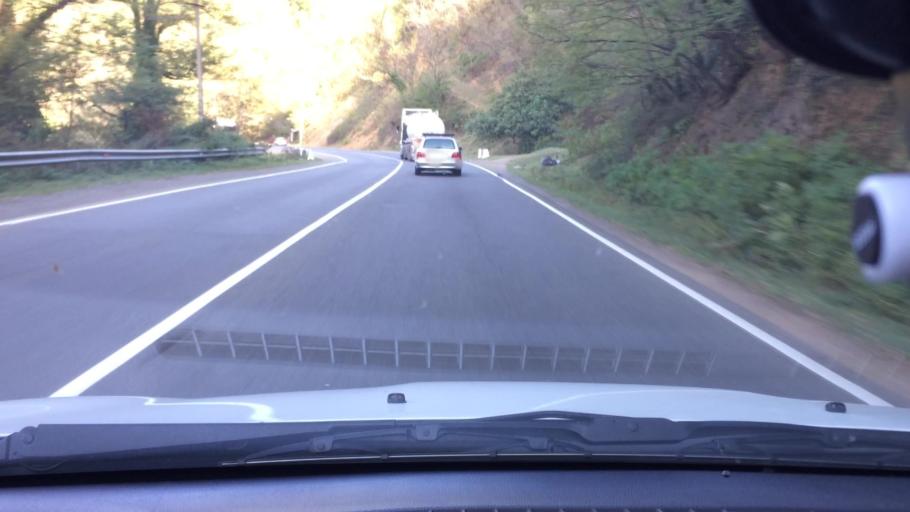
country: GE
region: Imereti
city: Kharagauli
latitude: 42.1013
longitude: 43.2271
